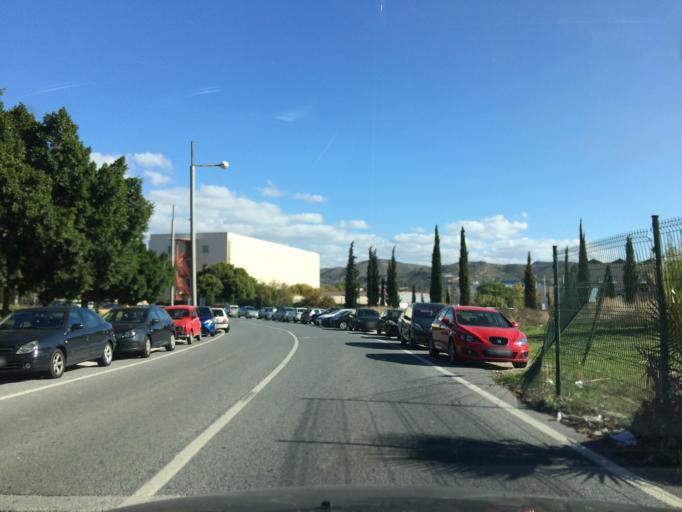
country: ES
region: Andalusia
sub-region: Provincia de Malaga
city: Estacion de Cartama
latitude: 36.7318
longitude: -4.5491
